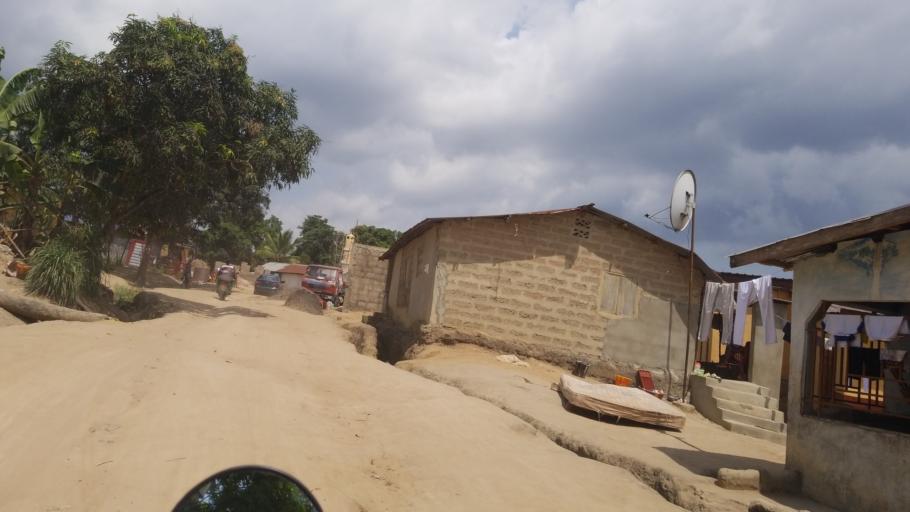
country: SL
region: Western Area
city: Waterloo
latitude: 8.3206
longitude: -13.0509
